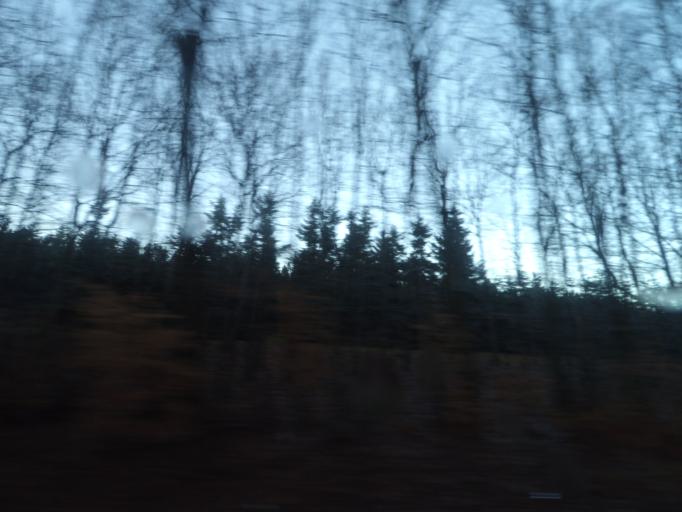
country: DK
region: Central Jutland
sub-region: Ikast-Brande Kommune
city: Brande
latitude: 56.0084
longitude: 9.0779
